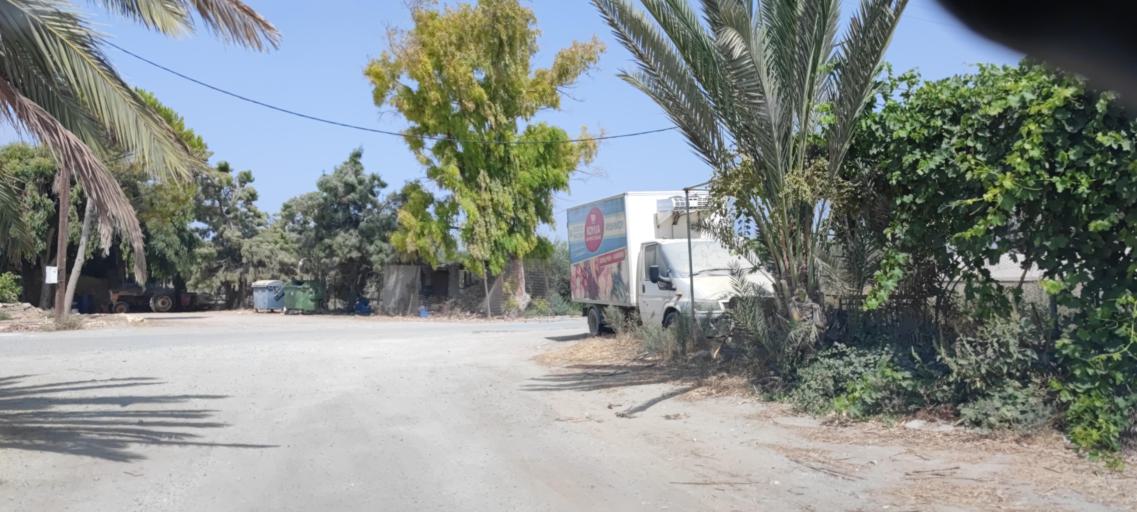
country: CY
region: Limassol
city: Pissouri
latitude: 34.6582
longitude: 32.7671
